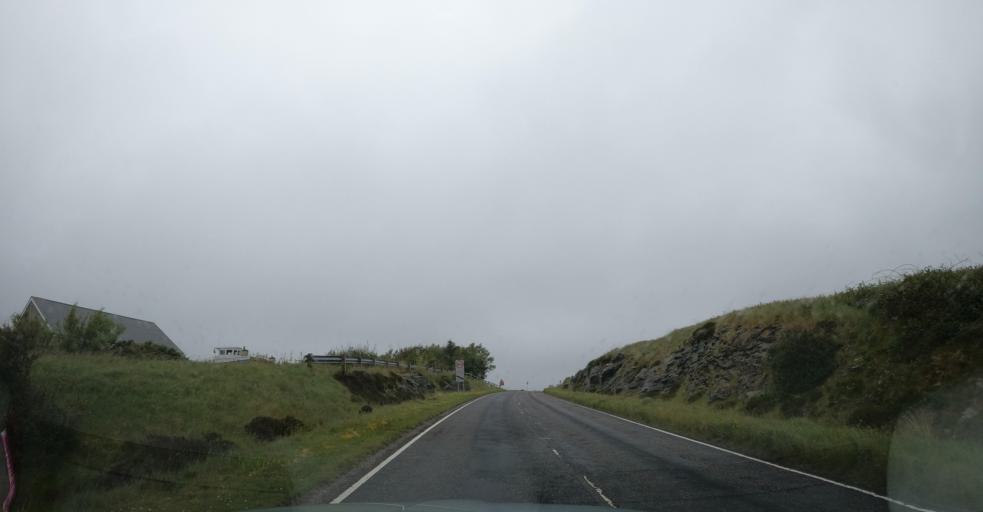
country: GB
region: Scotland
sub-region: Eilean Siar
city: Isle of North Uist
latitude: 57.6045
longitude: -7.1781
